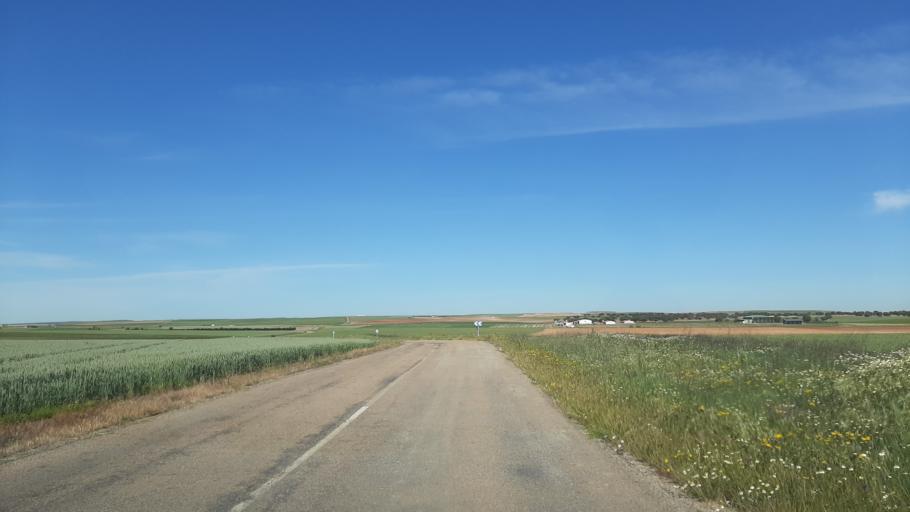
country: ES
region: Castille and Leon
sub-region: Provincia de Salamanca
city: Aldeaseca de Alba
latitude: 40.8249
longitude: -5.4268
